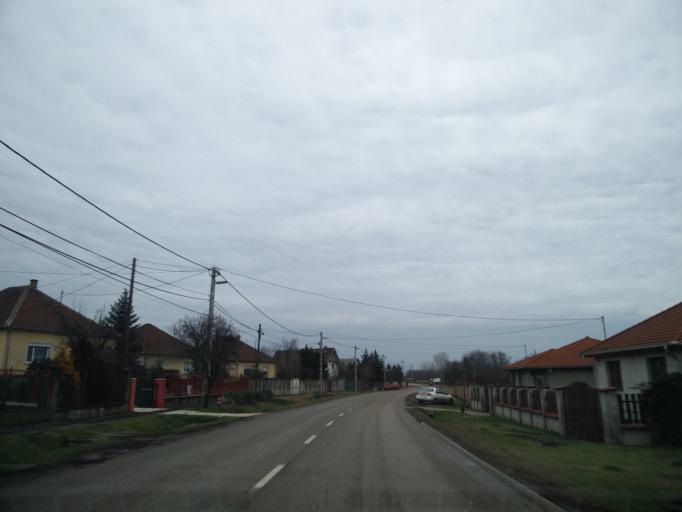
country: HU
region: Pest
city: Suelysap
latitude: 47.4529
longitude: 19.5376
